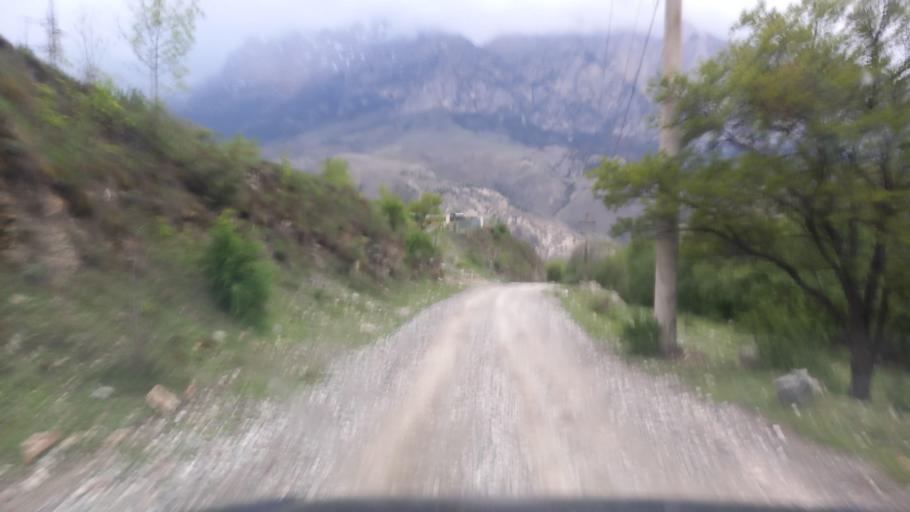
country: RU
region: North Ossetia
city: Mizur
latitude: 42.8498
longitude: 44.1560
